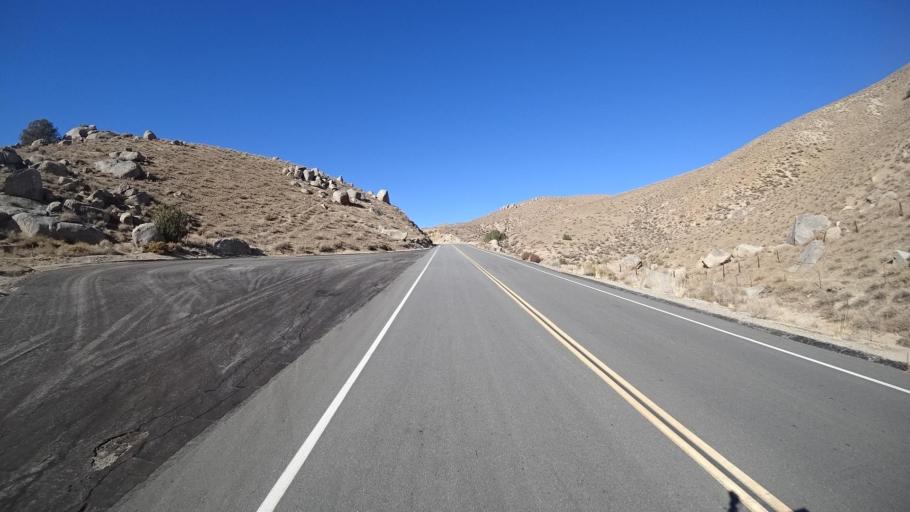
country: US
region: California
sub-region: Kern County
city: Weldon
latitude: 35.6754
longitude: -118.3564
